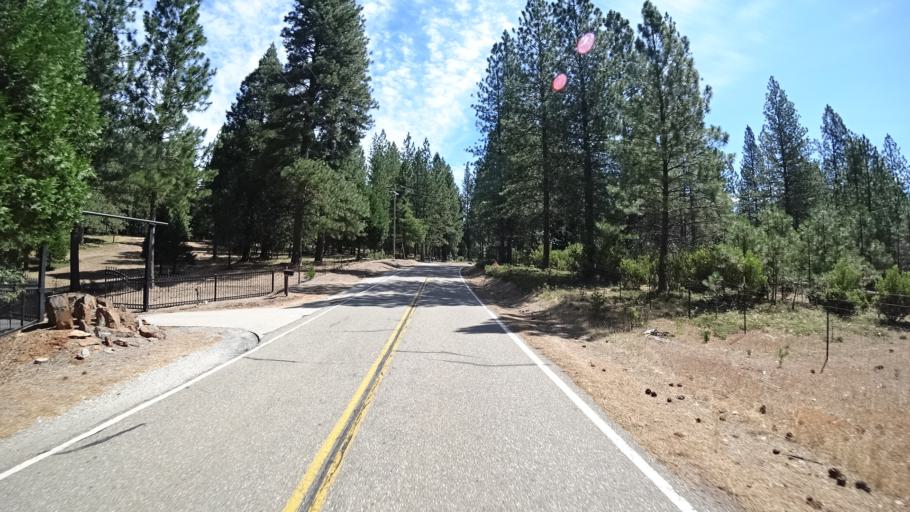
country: US
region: California
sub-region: Amador County
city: Pioneer
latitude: 38.3390
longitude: -120.5531
